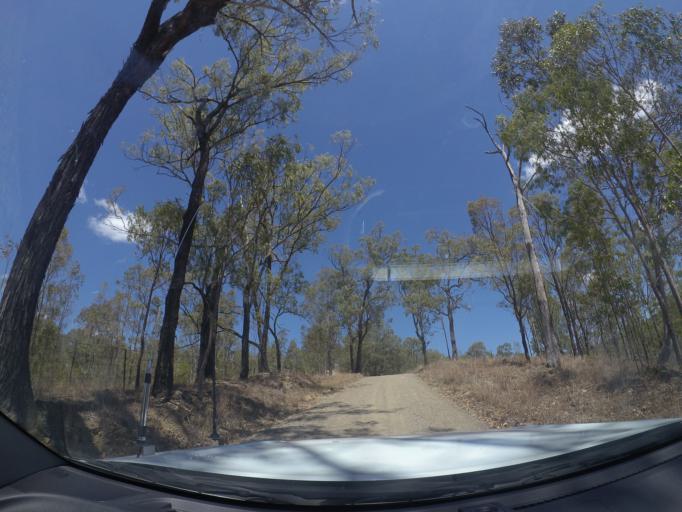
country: AU
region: Queensland
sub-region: Ipswich
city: Springfield Lakes
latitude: -27.8265
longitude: 152.8367
